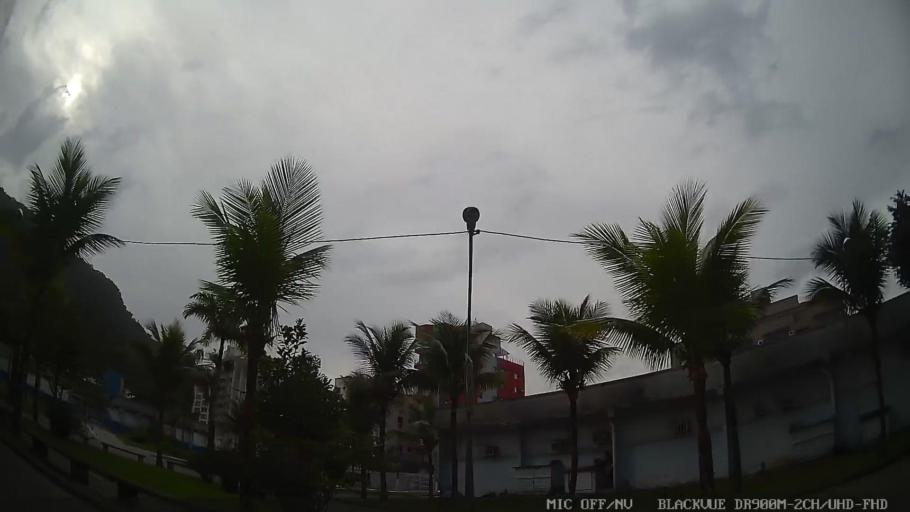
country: BR
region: Sao Paulo
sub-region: Guaruja
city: Guaruja
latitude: -23.9864
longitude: -46.2487
